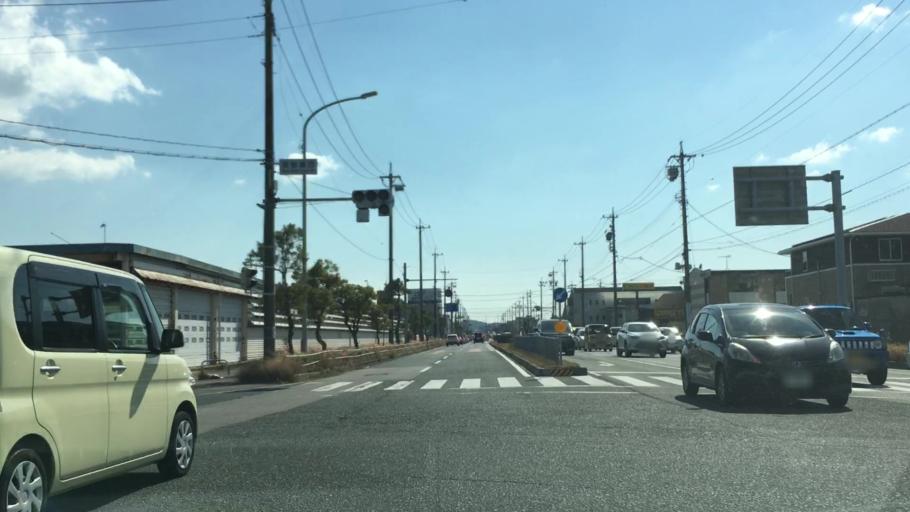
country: JP
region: Aichi
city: Gamagori
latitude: 34.8223
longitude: 137.2031
